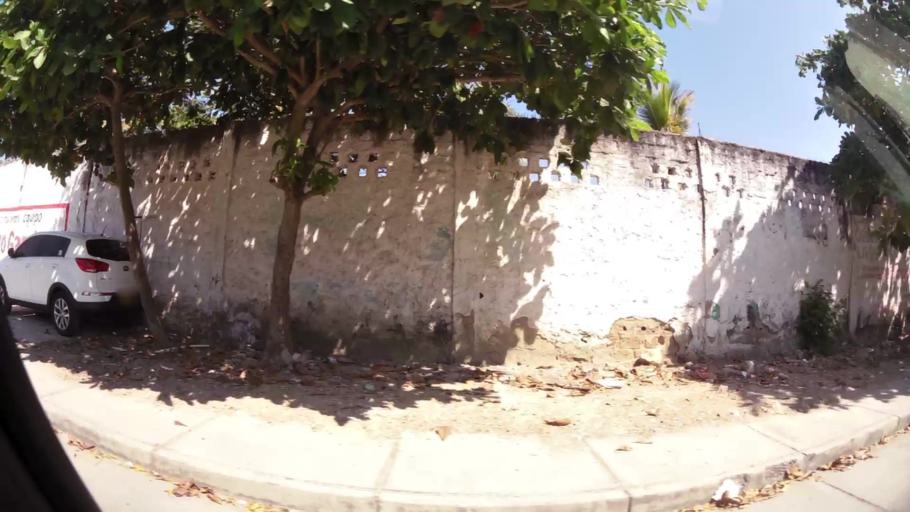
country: CO
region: Bolivar
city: Cartagena
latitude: 10.4413
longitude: -75.5221
